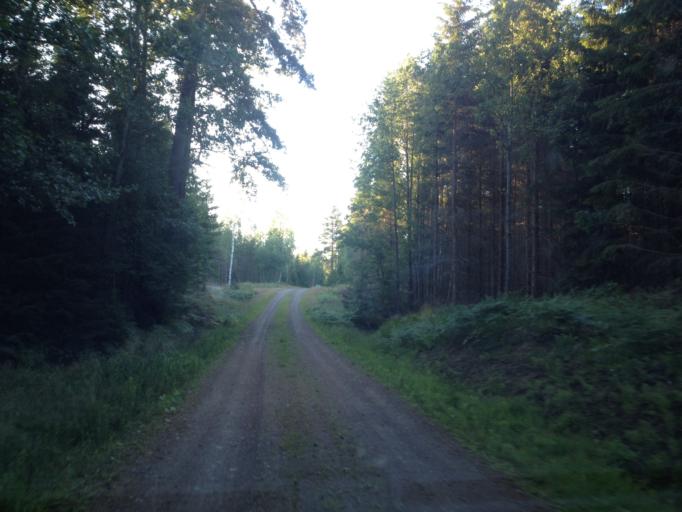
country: SE
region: Kalmar
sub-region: Vasterviks Kommun
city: Overum
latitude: 57.9944
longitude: 16.1693
